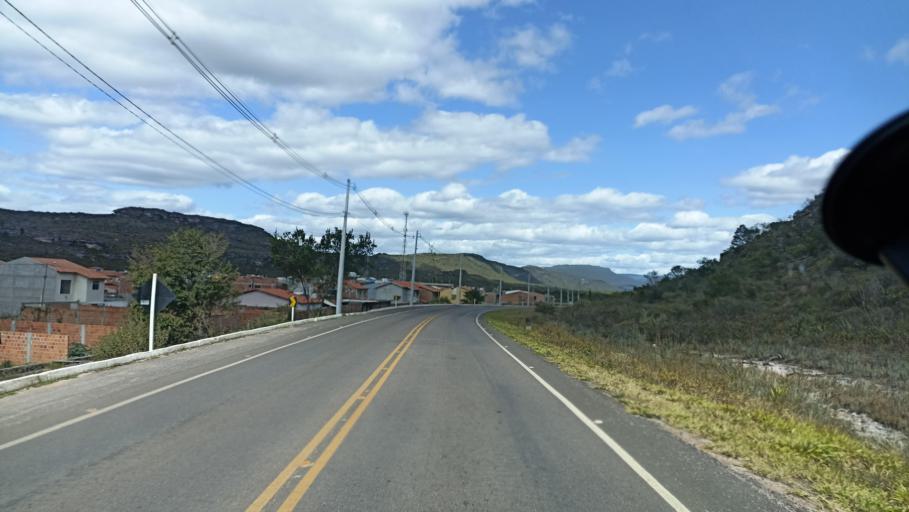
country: BR
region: Bahia
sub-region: Andarai
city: Vera Cruz
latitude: -13.0105
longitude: -41.3749
